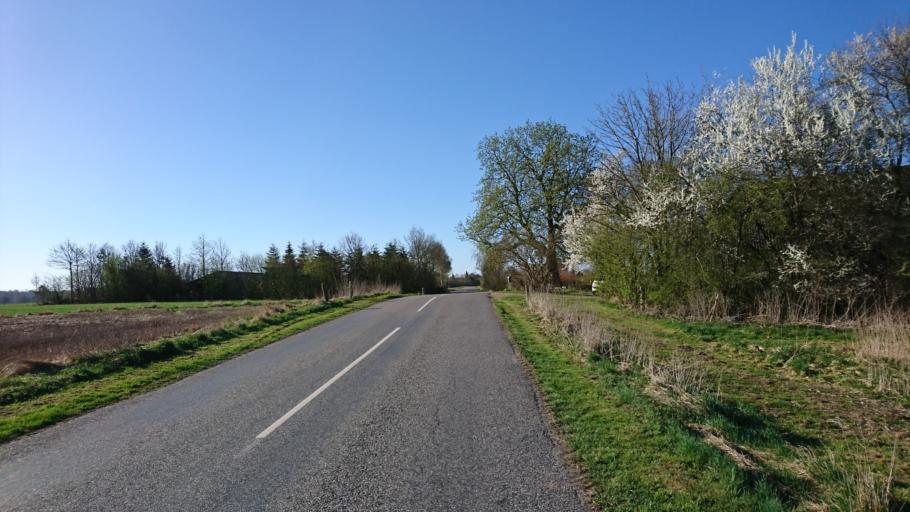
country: DK
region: Capital Region
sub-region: Frederikssund Kommune
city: Skibby
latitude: 55.7290
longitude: 11.9288
